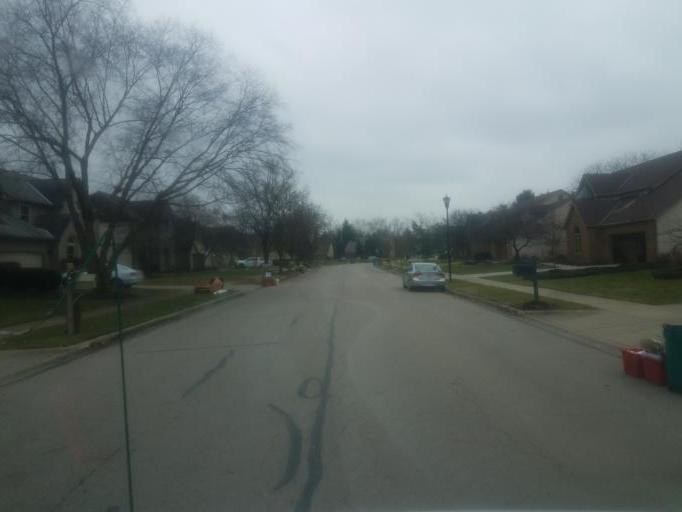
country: US
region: Ohio
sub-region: Franklin County
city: Westerville
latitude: 40.1300
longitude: -82.9590
